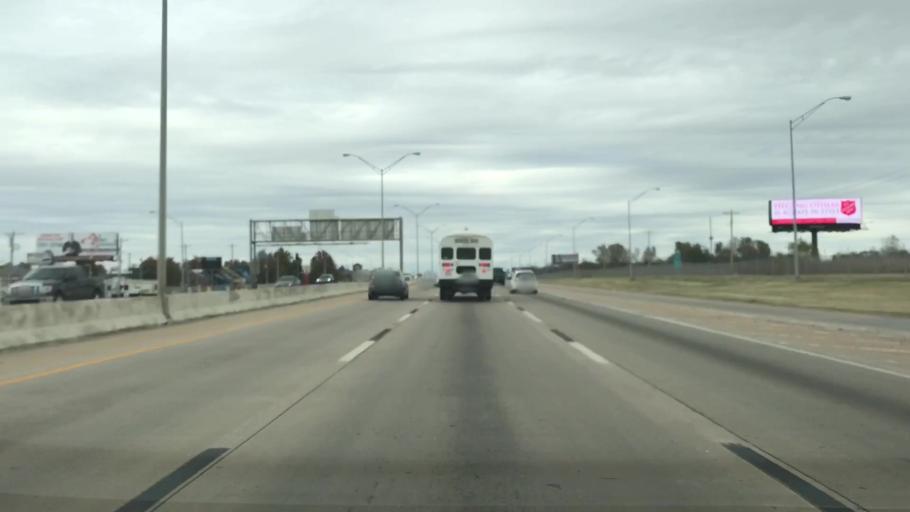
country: US
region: Oklahoma
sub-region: Cleveland County
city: Moore
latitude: 35.3665
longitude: -97.4948
